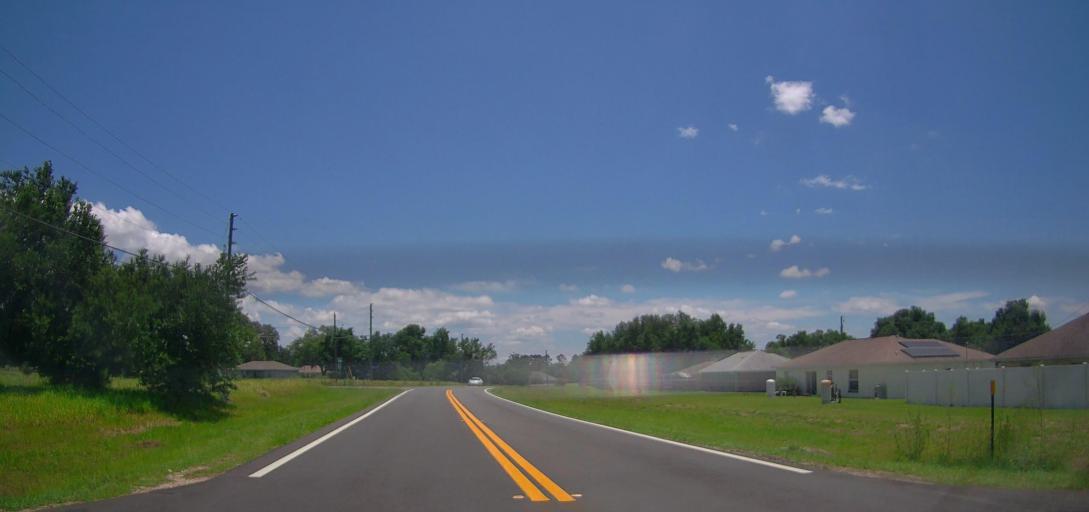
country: US
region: Florida
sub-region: Marion County
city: Silver Springs Shores
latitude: 29.1256
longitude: -82.0509
